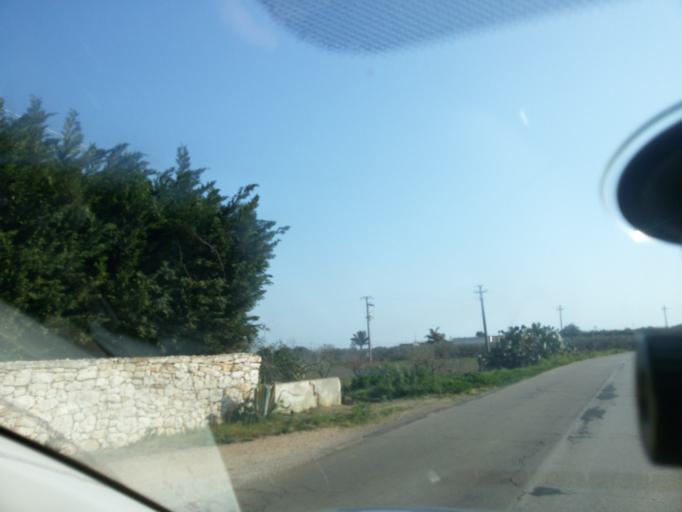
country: IT
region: Apulia
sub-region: Provincia di Brindisi
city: Mesagne
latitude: 40.5898
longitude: 17.8161
